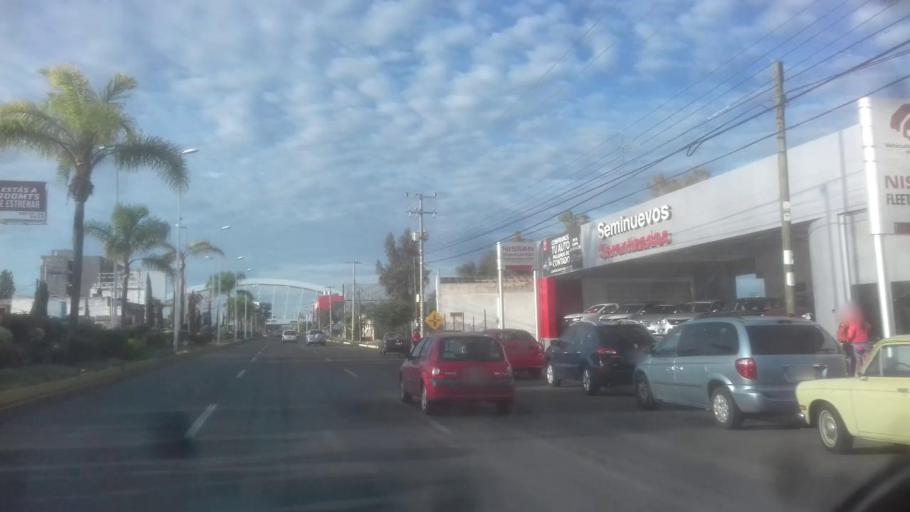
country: MX
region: Aguascalientes
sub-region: Aguascalientes
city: Aguascalientes
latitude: 21.8619
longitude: -102.2937
